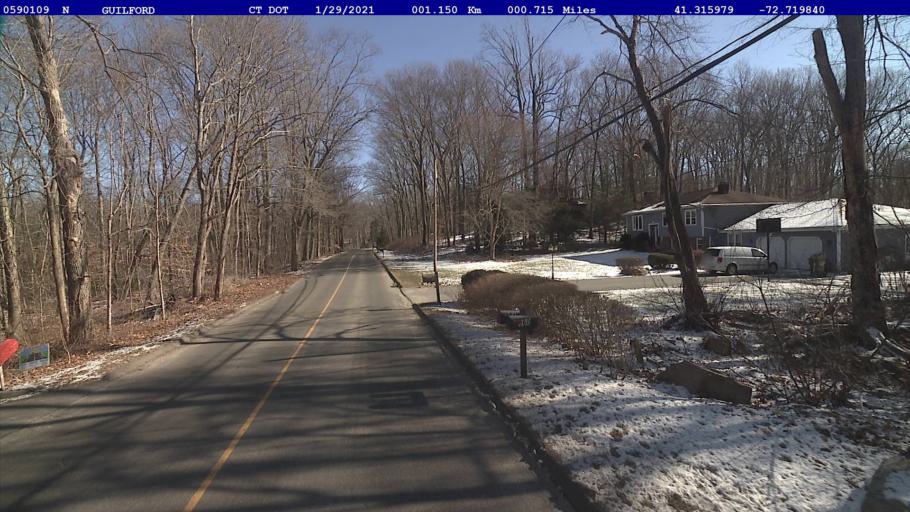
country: US
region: Connecticut
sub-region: New Haven County
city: Guilford
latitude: 41.3160
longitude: -72.7198
